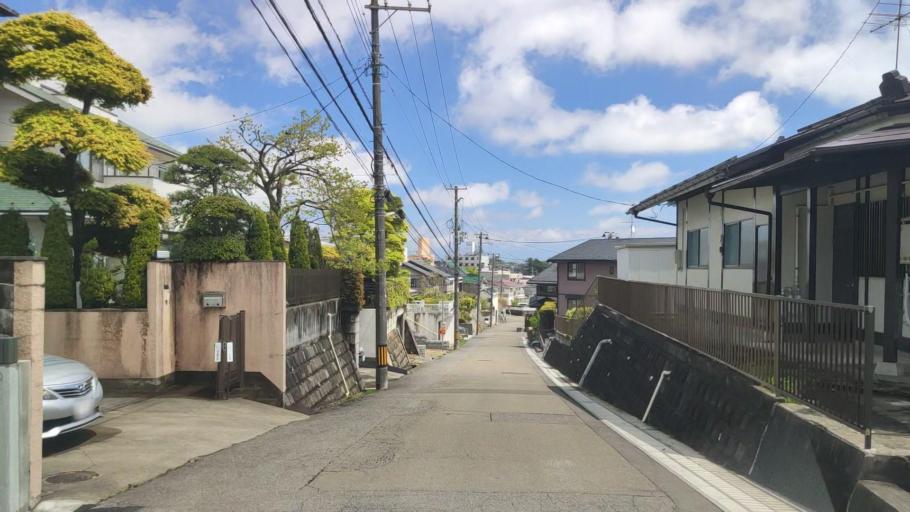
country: JP
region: Miyagi
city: Sendai
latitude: 38.2408
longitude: 140.8433
